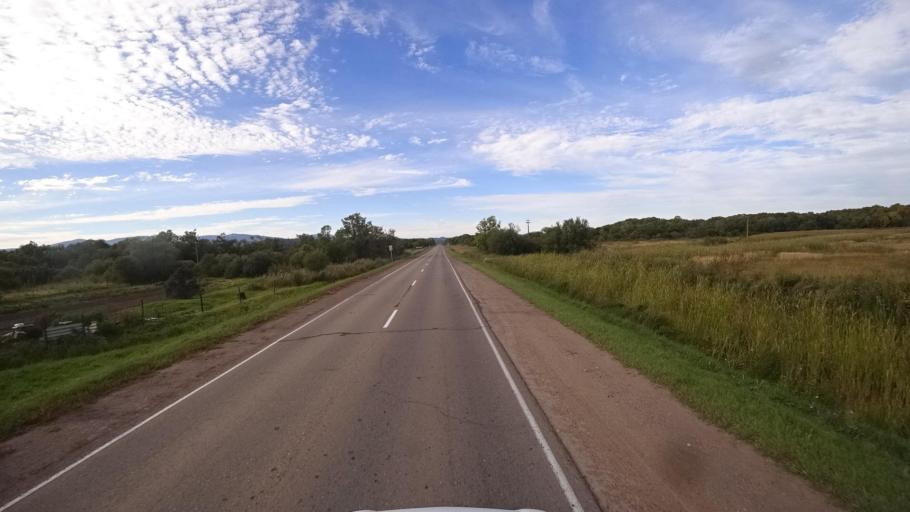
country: RU
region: Primorskiy
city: Dostoyevka
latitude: 44.2994
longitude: 133.4261
